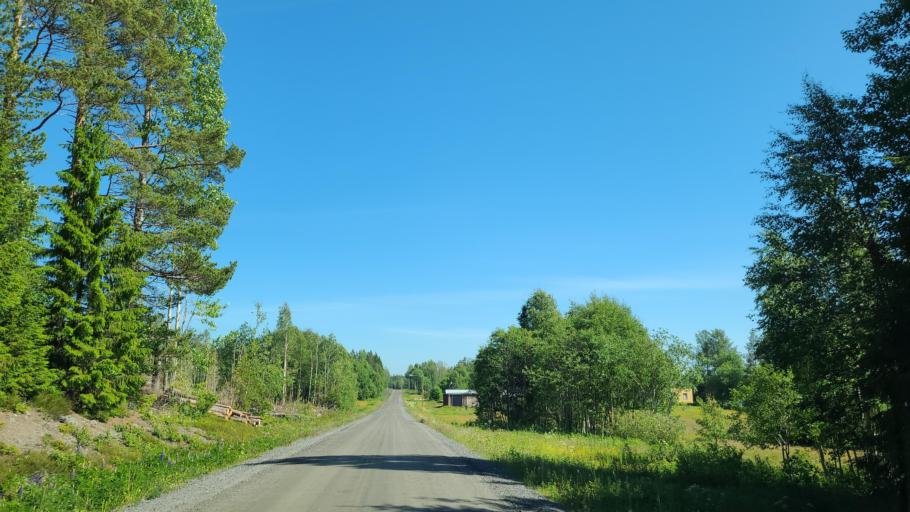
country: SE
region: Vaesterbotten
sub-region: Bjurholms Kommun
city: Bjurholm
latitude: 63.6415
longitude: 19.1323
